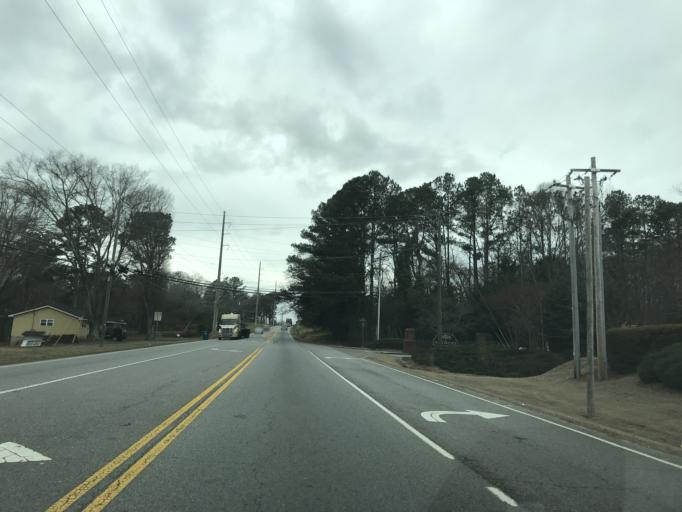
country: US
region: Georgia
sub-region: Fulton County
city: Milton
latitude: 34.1575
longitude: -84.2277
